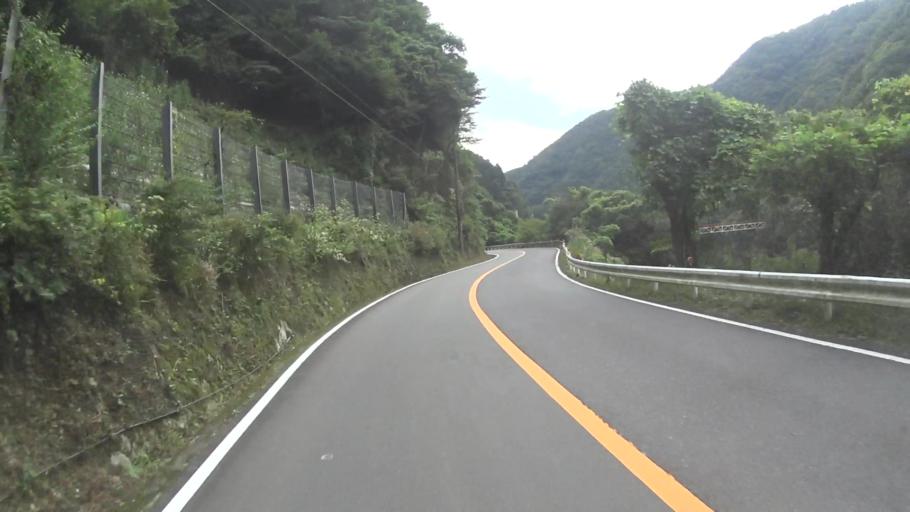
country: JP
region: Kyoto
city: Uji
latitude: 34.8804
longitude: 135.8481
